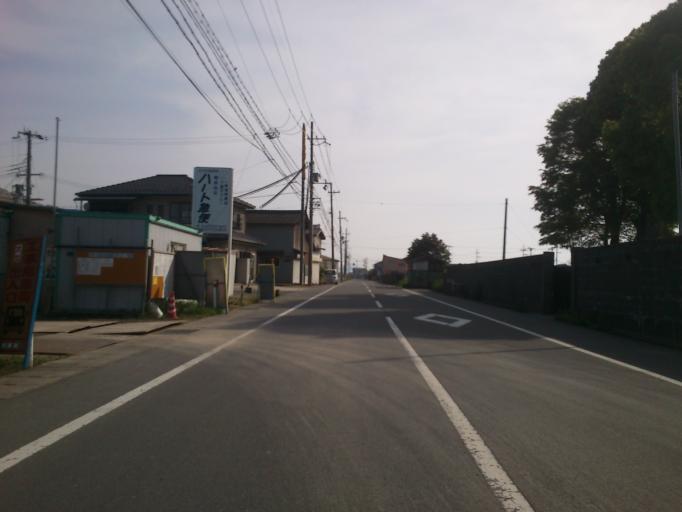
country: JP
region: Kyoto
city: Miyazu
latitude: 35.5819
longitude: 135.2022
